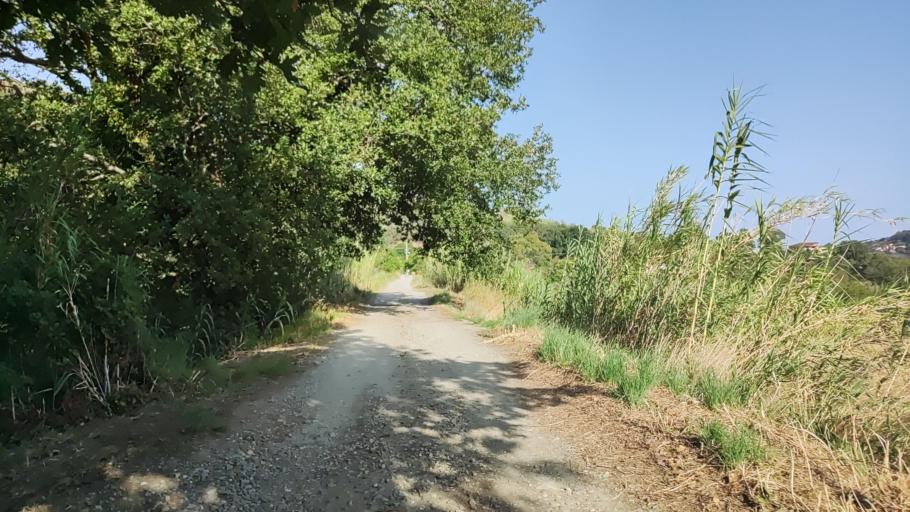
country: IT
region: Calabria
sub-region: Provincia di Reggio Calabria
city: Grotteria
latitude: 38.3495
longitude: 16.2578
